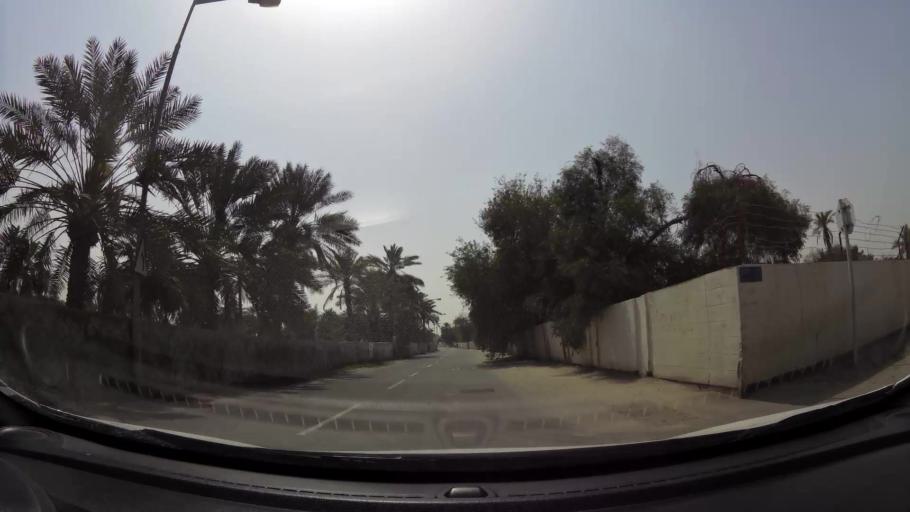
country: BH
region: Manama
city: Jidd Hafs
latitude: 26.2260
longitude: 50.5038
